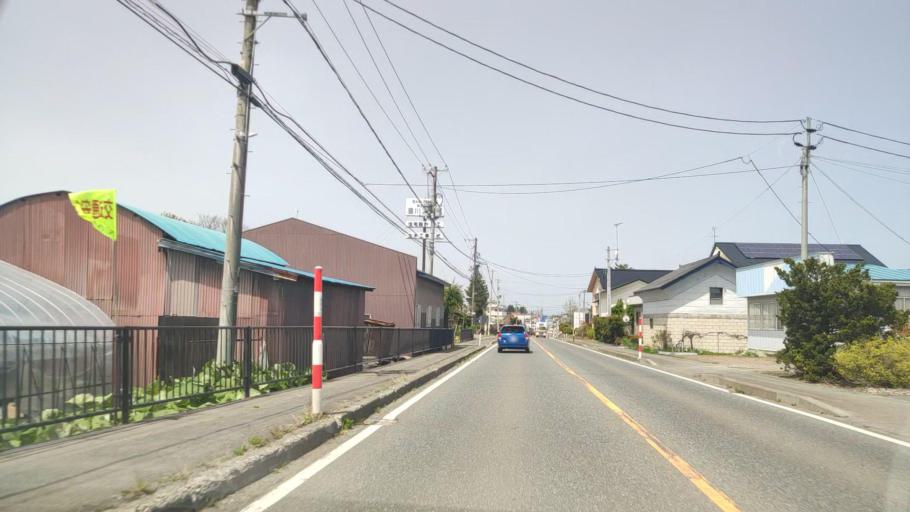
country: JP
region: Aomori
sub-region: Misawa Shi
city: Inuotose
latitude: 40.6531
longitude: 141.1946
